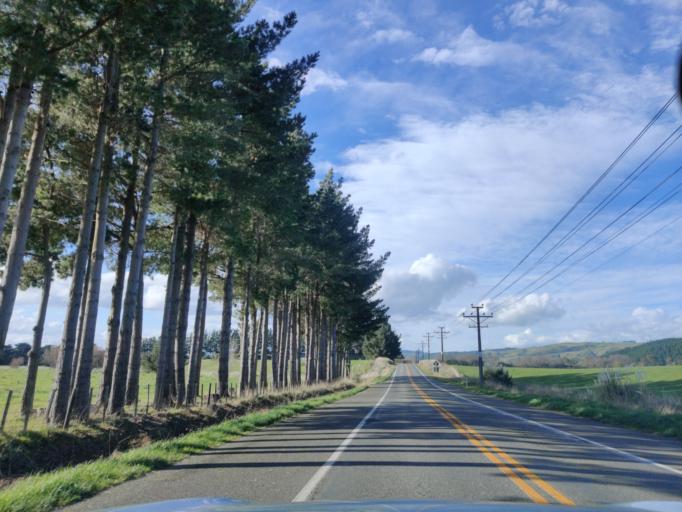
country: NZ
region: Manawatu-Wanganui
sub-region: Palmerston North City
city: Palmerston North
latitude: -40.3382
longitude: 175.7223
